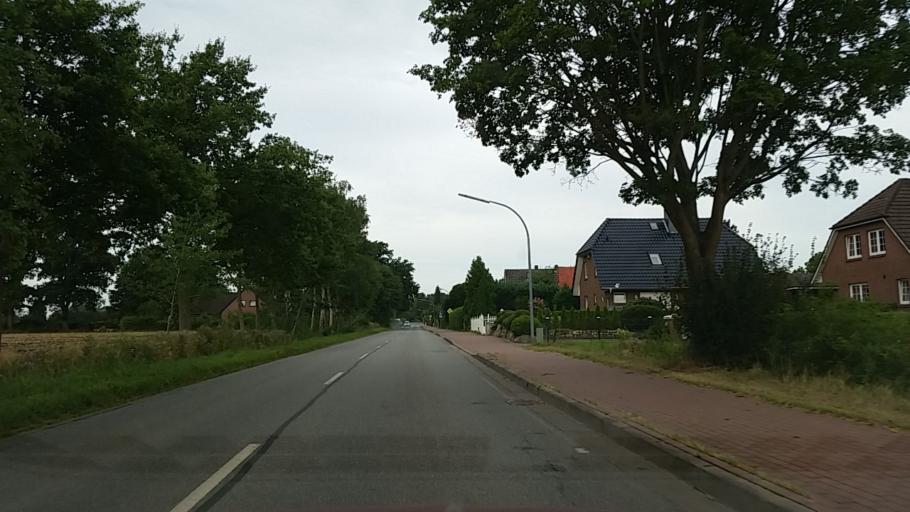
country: DE
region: Schleswig-Holstein
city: Bonningstedt
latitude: 53.6927
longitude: 9.9331
